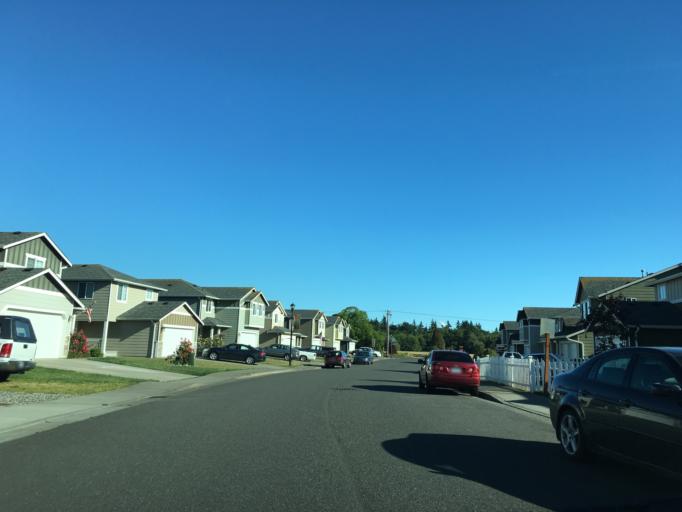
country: US
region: Washington
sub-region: Whatcom County
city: Birch Bay
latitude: 48.9082
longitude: -122.7415
